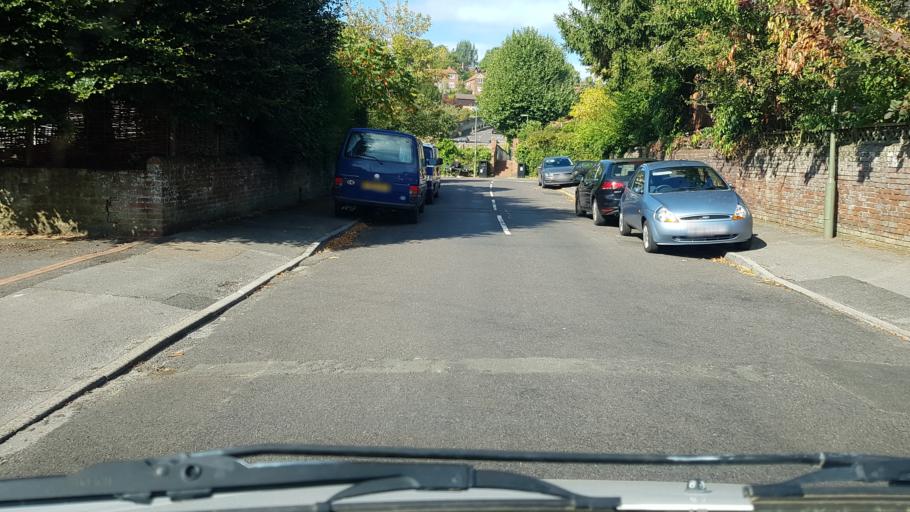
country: GB
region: England
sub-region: Surrey
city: Godalming
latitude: 51.1945
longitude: -0.6063
